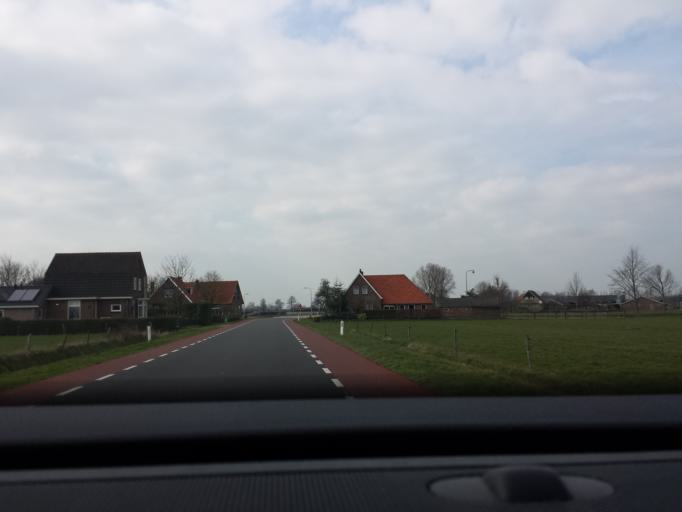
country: NL
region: Gelderland
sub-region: Oost Gelre
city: Lichtenvoorde
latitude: 52.0172
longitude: 6.5005
